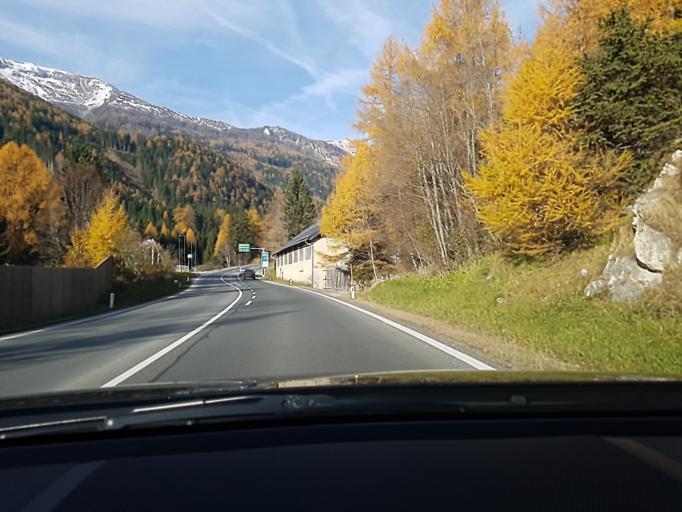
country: AT
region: Salzburg
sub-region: Politischer Bezirk Tamsweg
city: Mauterndorf
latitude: 47.1433
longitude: 13.6640
